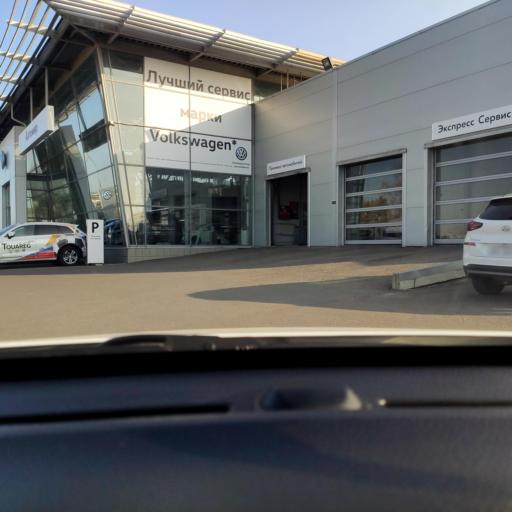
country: RU
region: Voronezj
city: Somovo
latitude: 51.6753
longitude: 39.3022
